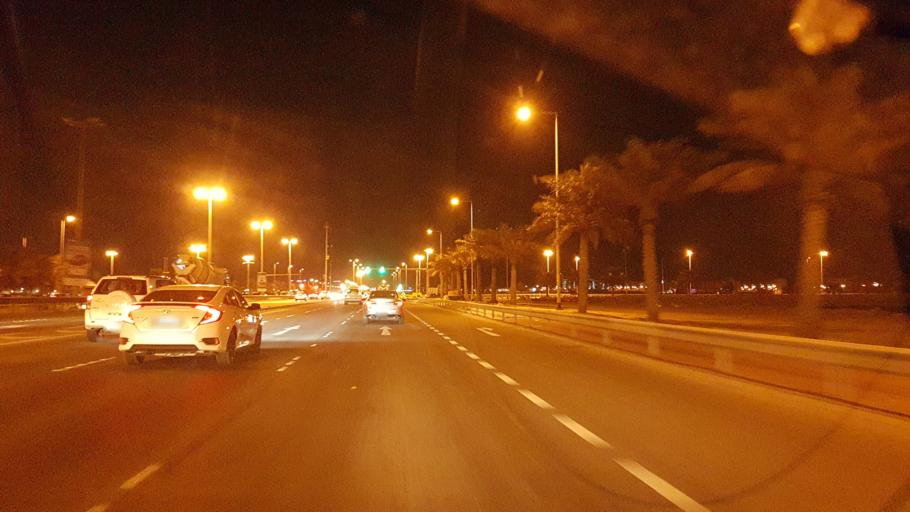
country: BH
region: Muharraq
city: Al Hadd
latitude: 26.2524
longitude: 50.6597
